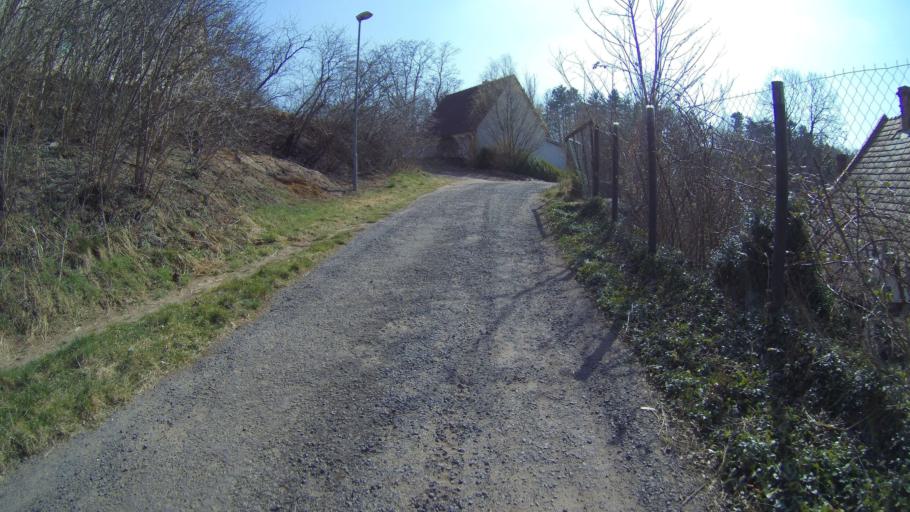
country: CZ
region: Ustecky
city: Mecholupy
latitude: 50.2885
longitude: 13.5763
